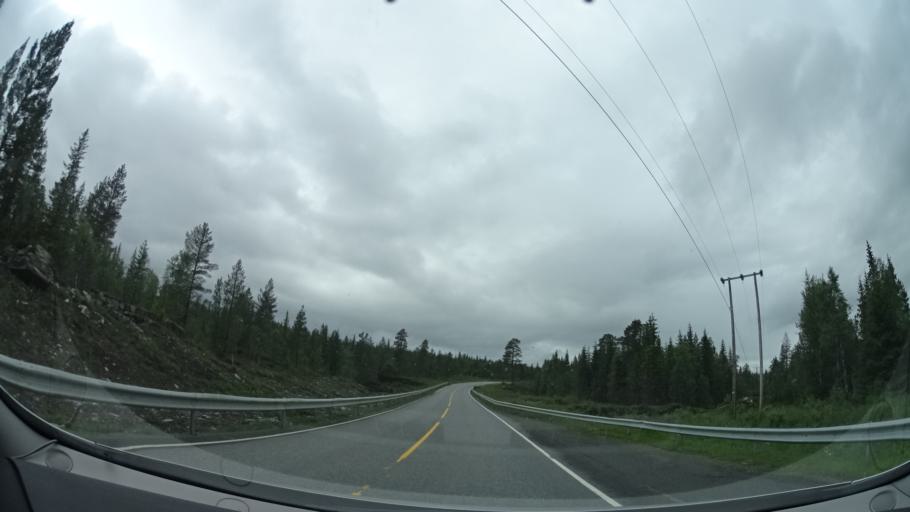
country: NO
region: Nord-Trondelag
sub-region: Meraker
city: Meraker
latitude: 63.3485
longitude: 12.0094
